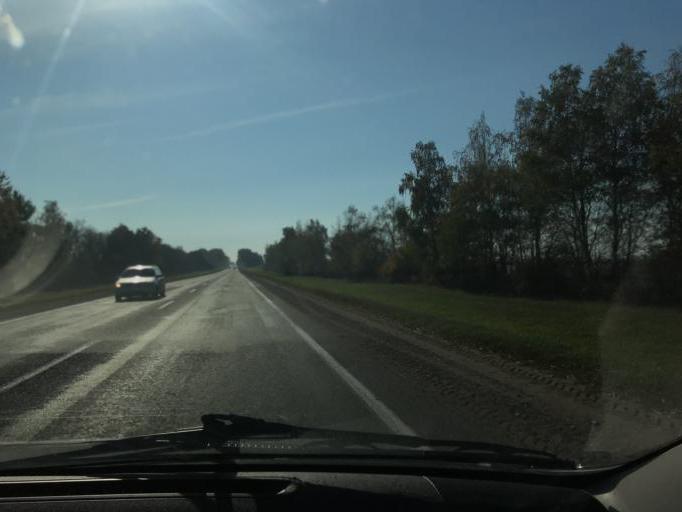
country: BY
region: Minsk
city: Salihorsk
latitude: 52.8463
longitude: 27.4659
